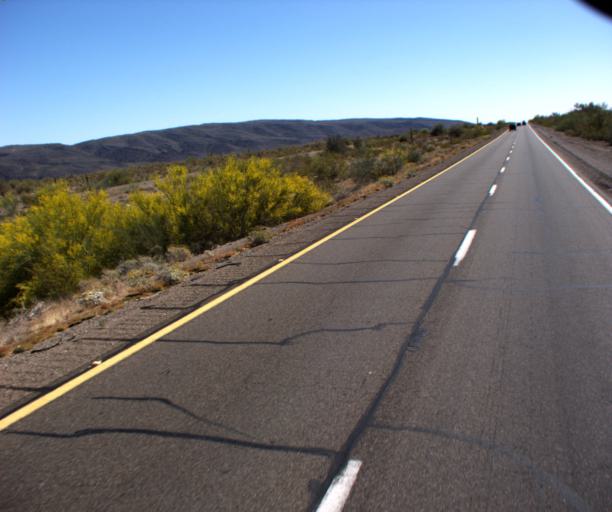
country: US
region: Arizona
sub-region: La Paz County
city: Quartzsite
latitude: 33.6545
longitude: -113.9528
